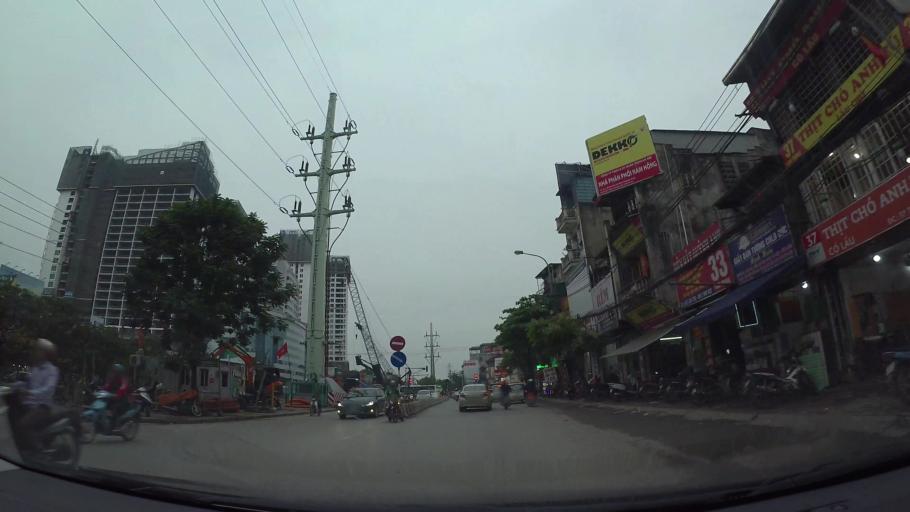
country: VN
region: Ha Noi
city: Hai BaTrung
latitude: 20.9954
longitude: 105.8627
